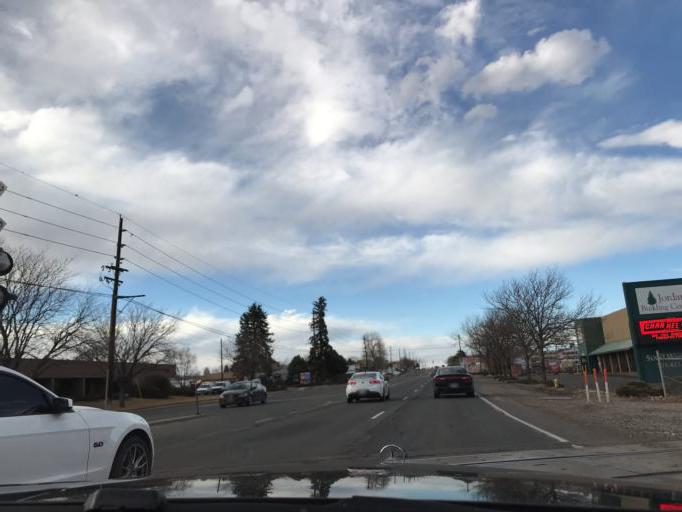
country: US
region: Colorado
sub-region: Jefferson County
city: Applewood
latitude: 39.7865
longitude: -105.1378
